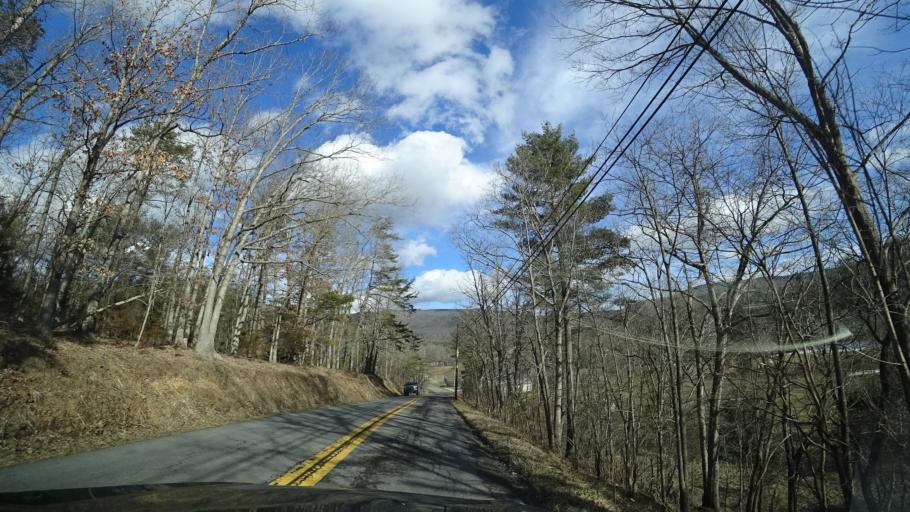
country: US
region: Virginia
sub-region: Shenandoah County
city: Basye
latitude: 38.8773
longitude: -78.8726
